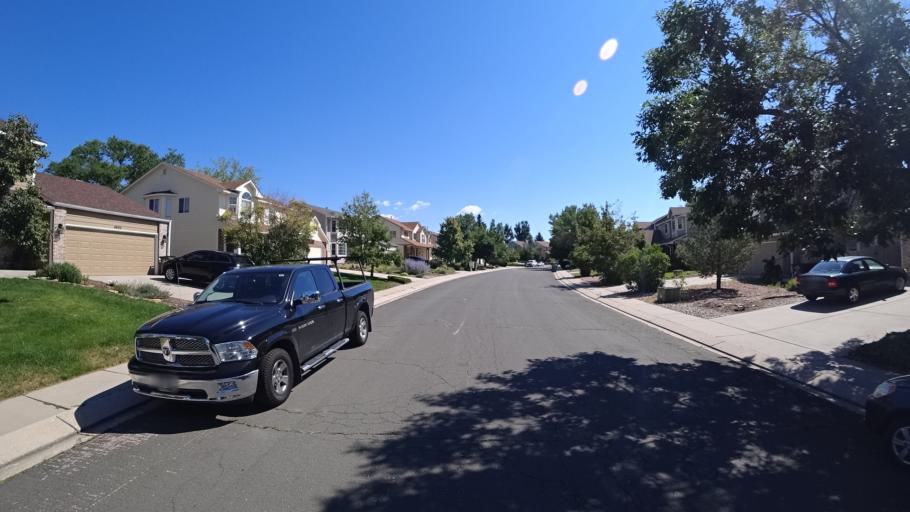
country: US
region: Colorado
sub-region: El Paso County
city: Black Forest
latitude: 38.9440
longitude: -104.7486
